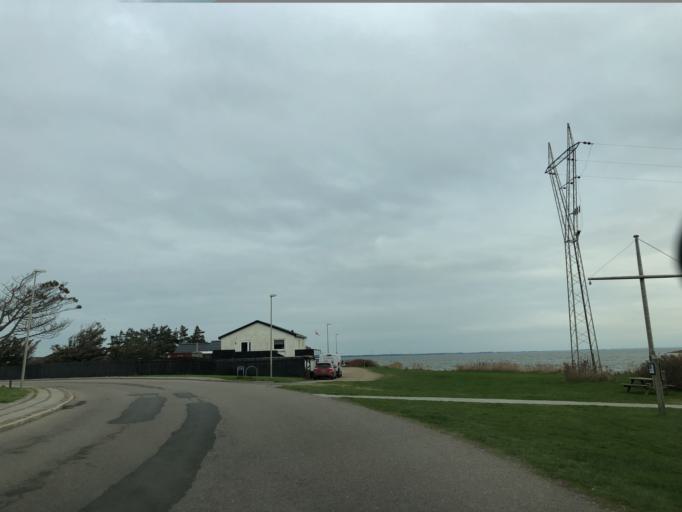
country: DK
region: Central Jutland
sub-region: Holstebro Kommune
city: Ulfborg
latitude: 56.3729
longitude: 8.1257
